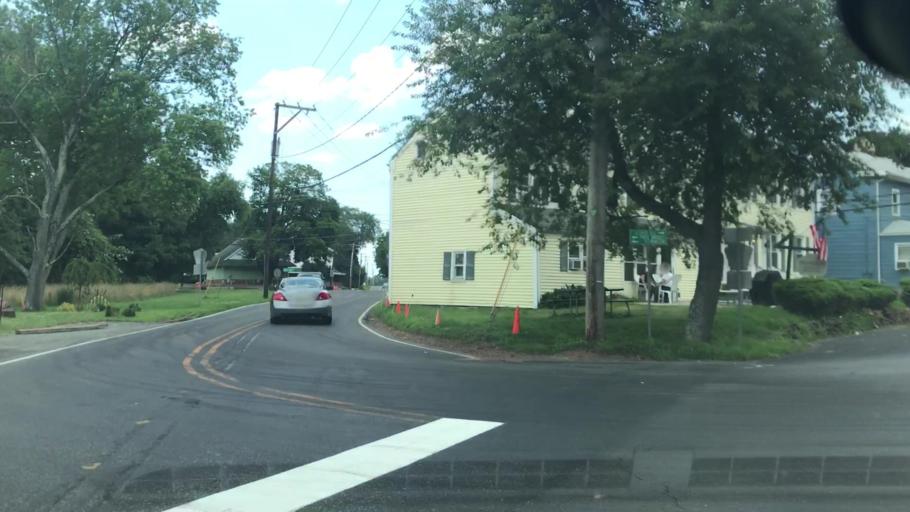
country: US
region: New Jersey
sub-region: Hunterdon County
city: Flemington
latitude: 40.4778
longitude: -74.8180
